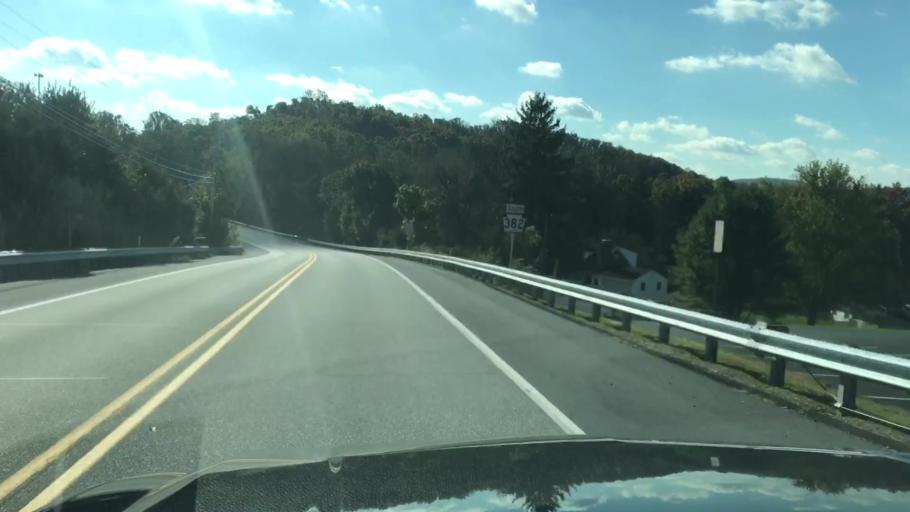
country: US
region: Pennsylvania
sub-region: Cumberland County
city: Lower Allen
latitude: 40.1710
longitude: -76.8898
